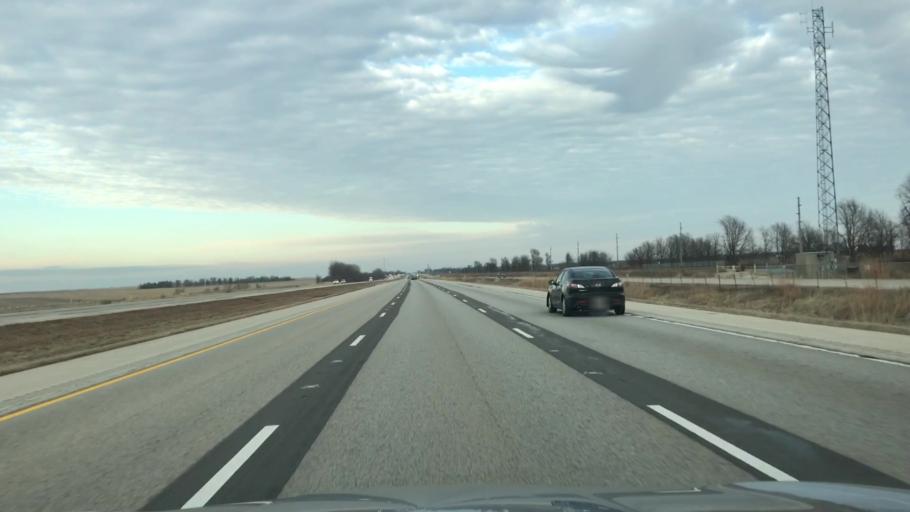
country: US
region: Illinois
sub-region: Sangamon County
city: Williamsville
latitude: 40.0343
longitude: -89.4722
